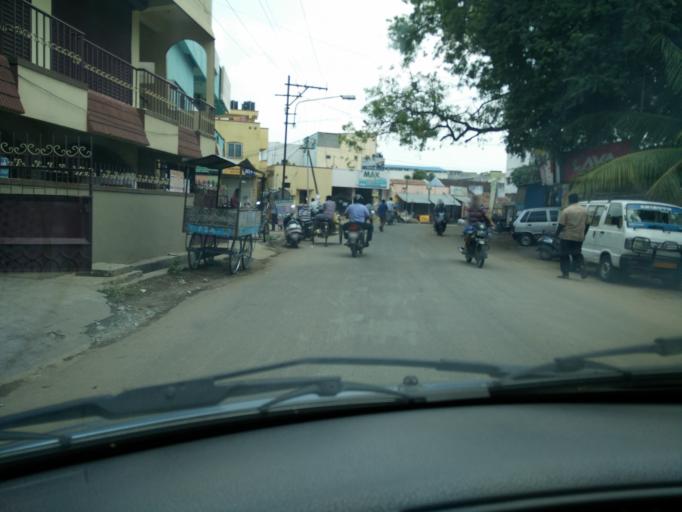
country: IN
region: Tamil Nadu
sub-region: Coimbatore
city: Coimbatore
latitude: 11.0354
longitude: 76.9757
